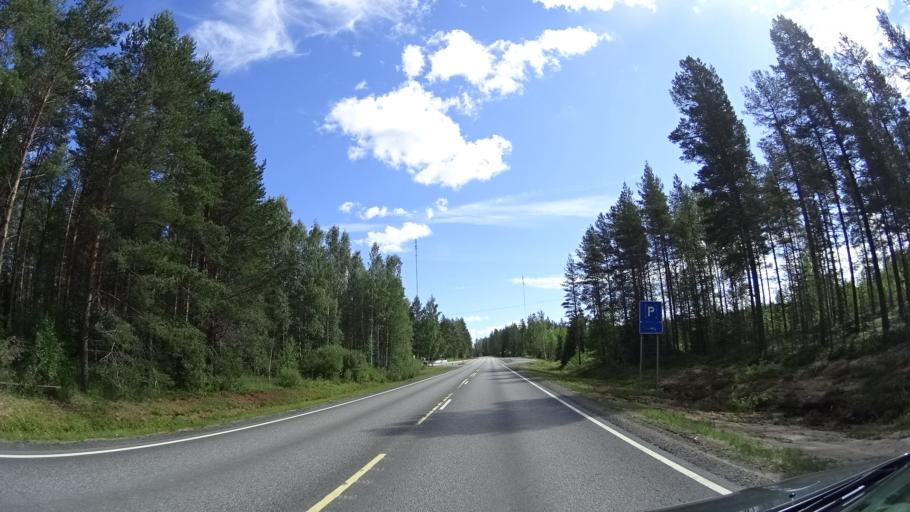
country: FI
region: Pirkanmaa
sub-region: Luoteis-Pirkanmaa
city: Kihnioe
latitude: 62.2007
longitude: 23.2085
